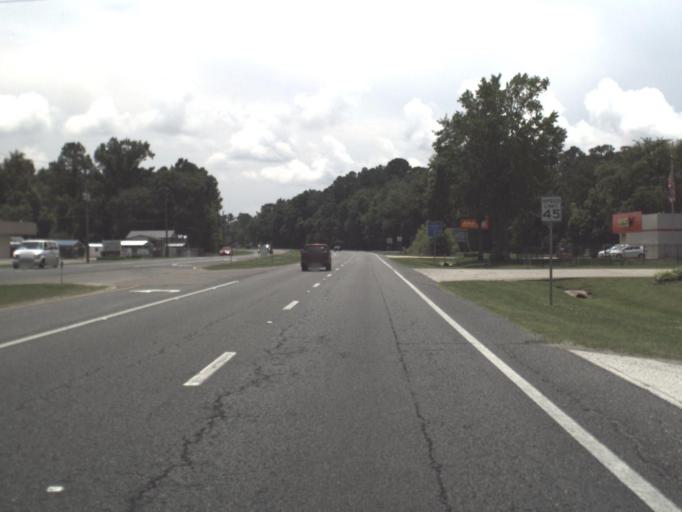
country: US
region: Florida
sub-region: Nassau County
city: Callahan
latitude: 30.5577
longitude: -81.8247
